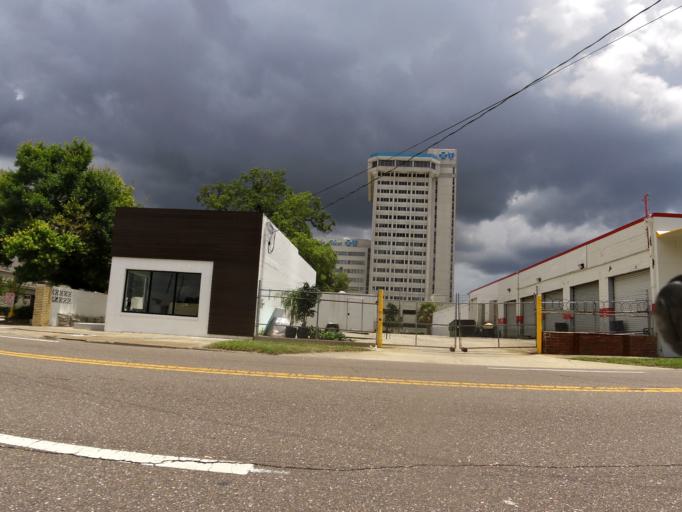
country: US
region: Florida
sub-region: Duval County
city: Jacksonville
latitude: 30.3206
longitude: -81.6781
